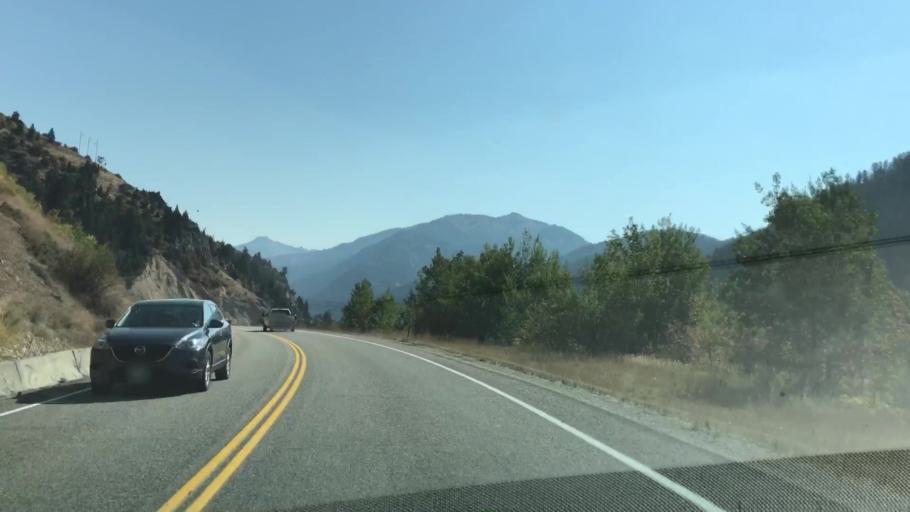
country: US
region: Idaho
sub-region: Teton County
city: Victor
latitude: 43.3188
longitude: -111.1527
